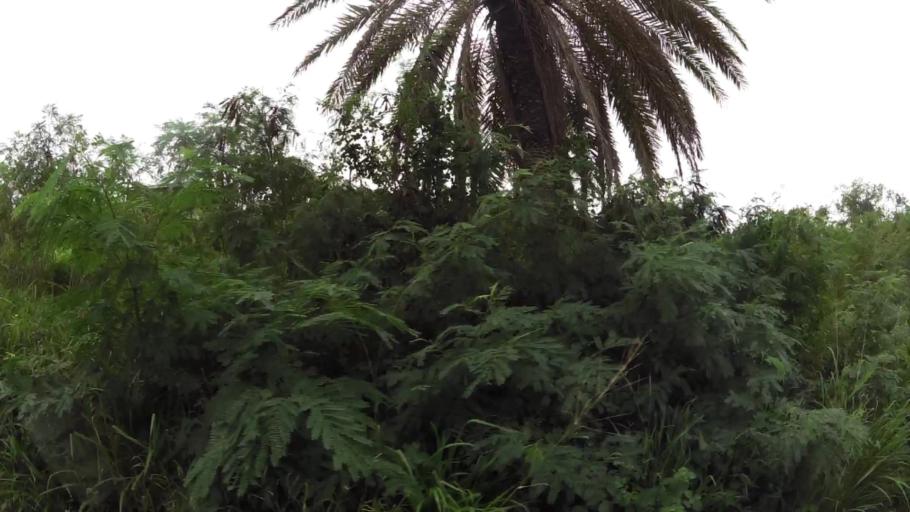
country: AG
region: Saint John
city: Potters Village
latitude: 17.0896
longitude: -61.8101
